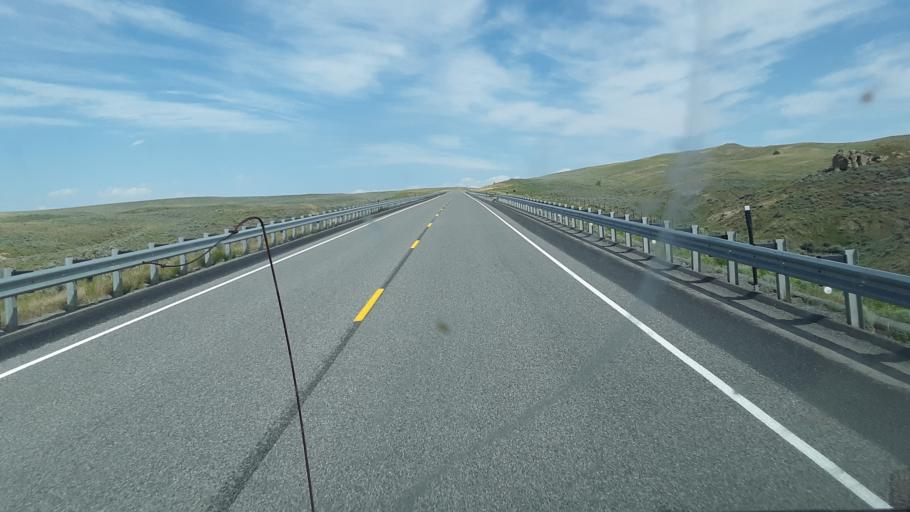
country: US
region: Wyoming
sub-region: Park County
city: Cody
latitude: 44.2523
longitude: -108.8611
